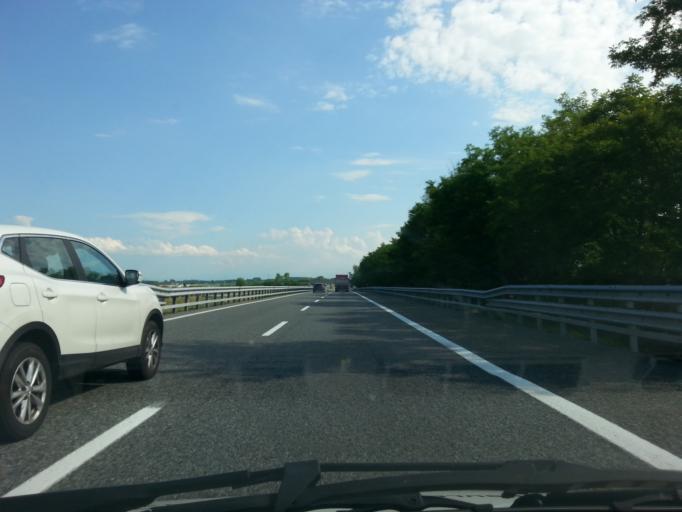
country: IT
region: Piedmont
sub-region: Provincia di Cuneo
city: Caramagna Piemonte
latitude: 44.7980
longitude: 7.7524
